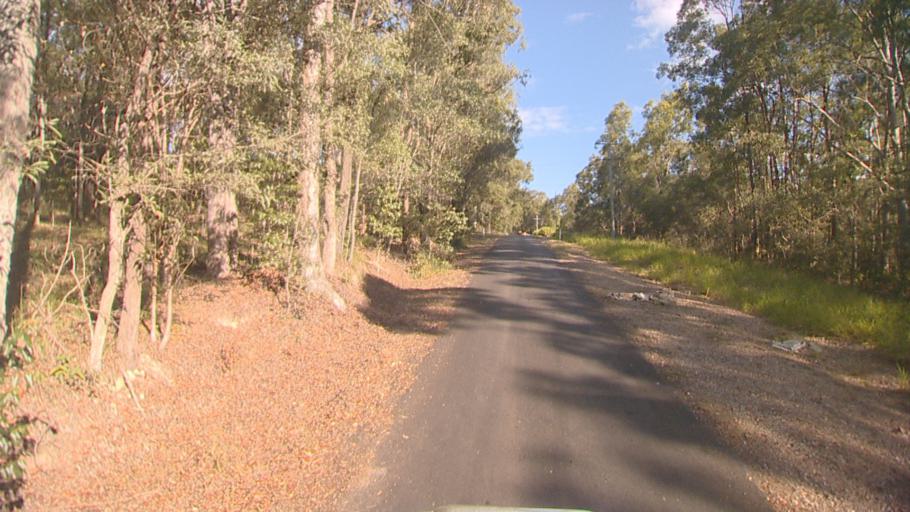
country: AU
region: Queensland
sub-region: Logan
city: Windaroo
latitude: -27.7408
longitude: 153.1652
